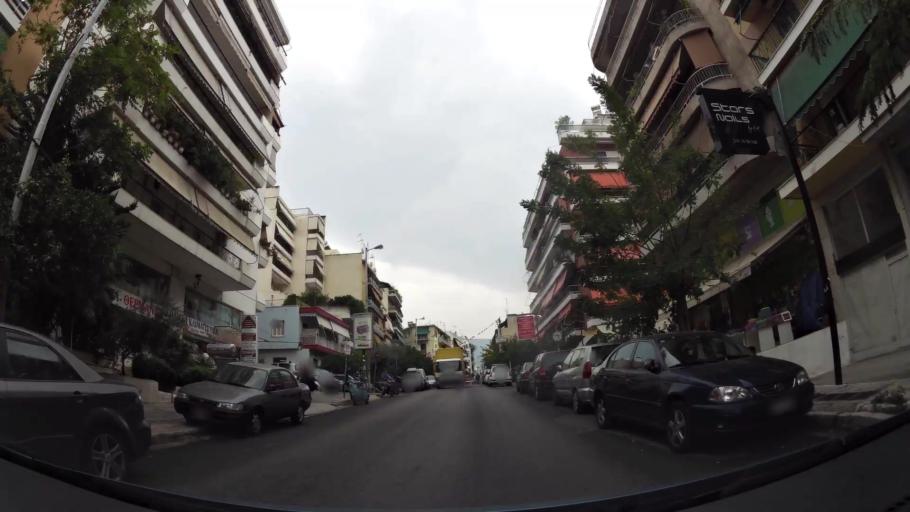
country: GR
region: Attica
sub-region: Nomarchia Athinas
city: Vyronas
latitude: 37.9637
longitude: 23.7577
